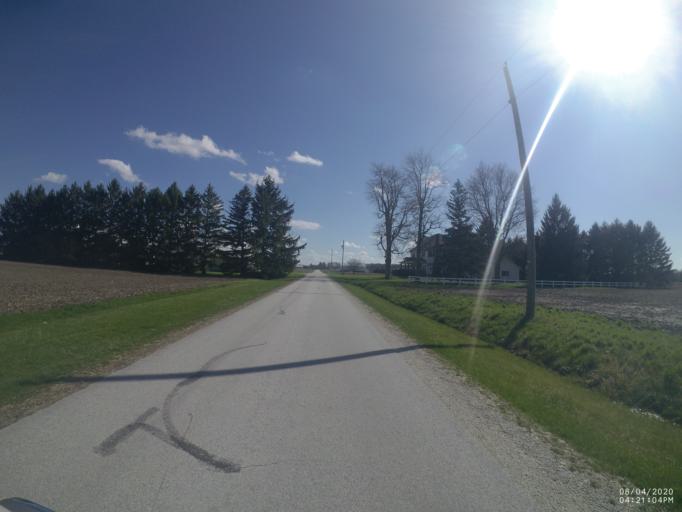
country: US
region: Ohio
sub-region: Sandusky County
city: Stony Prairie
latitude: 41.2876
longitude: -83.2166
